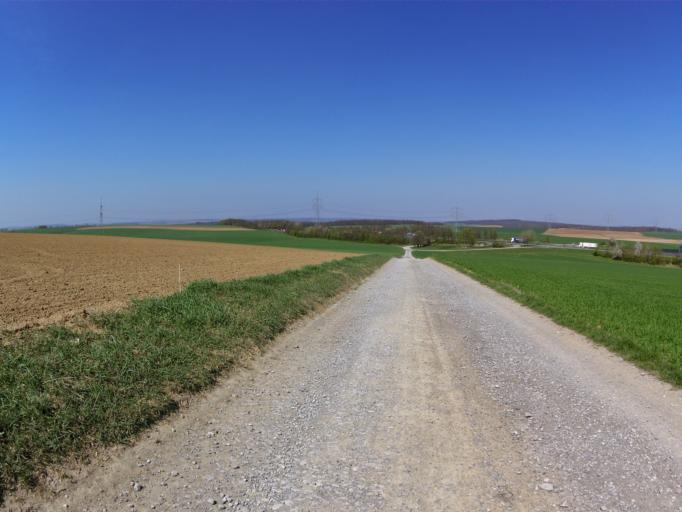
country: DE
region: Bavaria
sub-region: Regierungsbezirk Unterfranken
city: Biebelried
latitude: 49.7877
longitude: 10.0642
